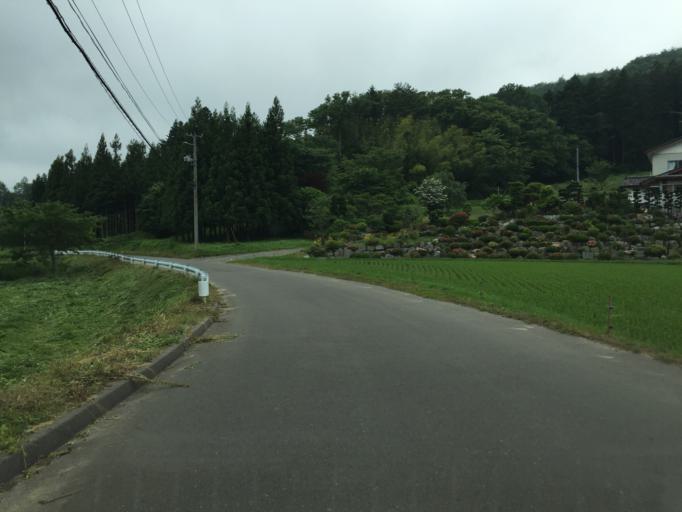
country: JP
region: Miyagi
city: Marumori
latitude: 37.8036
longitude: 140.7436
